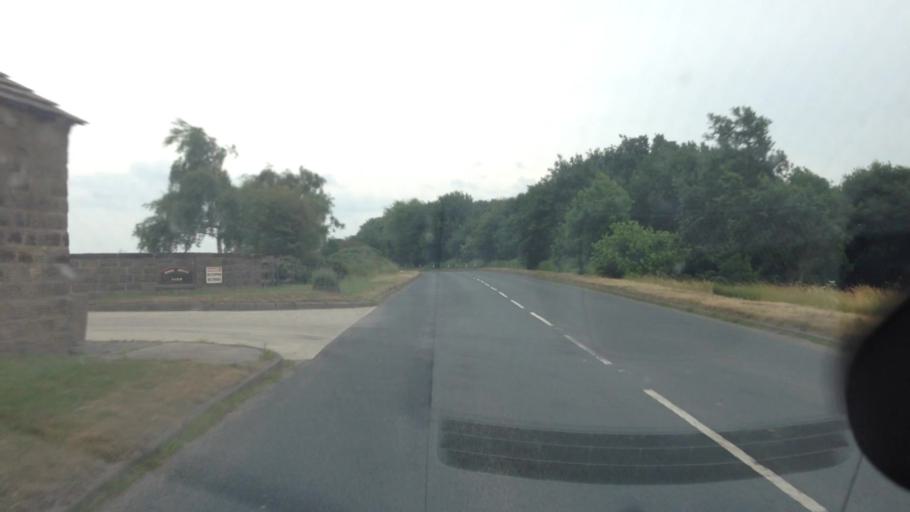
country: GB
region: England
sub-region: City and Borough of Wakefield
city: Woolley
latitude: 53.6129
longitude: -1.5351
